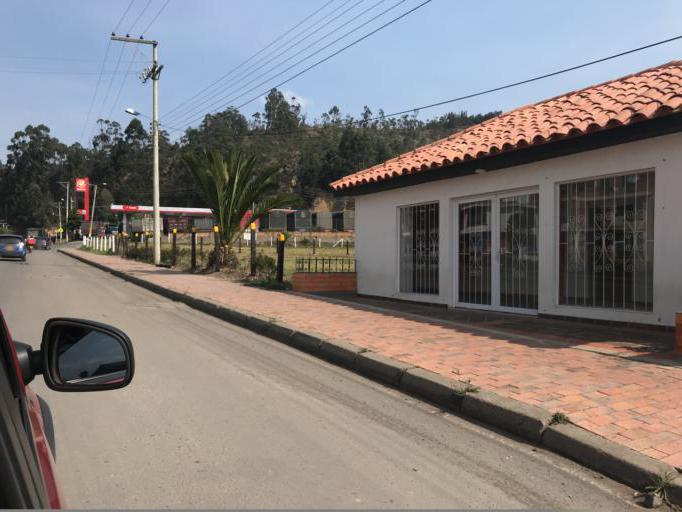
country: CO
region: Boyaca
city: Samaca
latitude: 5.4925
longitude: -73.4813
